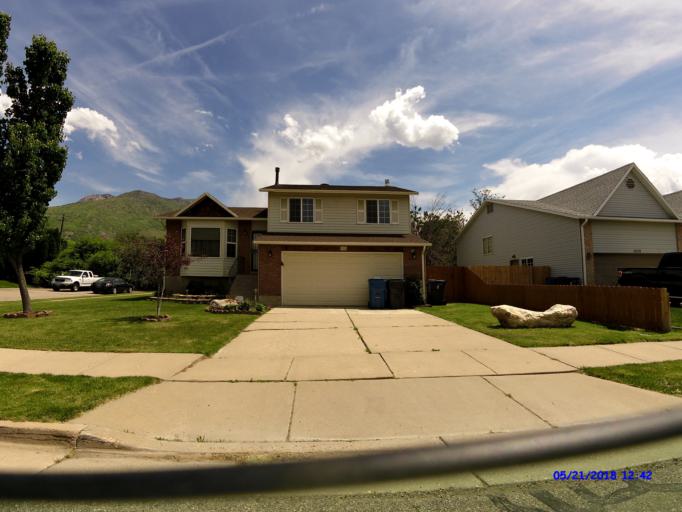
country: US
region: Utah
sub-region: Weber County
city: Washington Terrace
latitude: 41.1719
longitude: -111.9497
